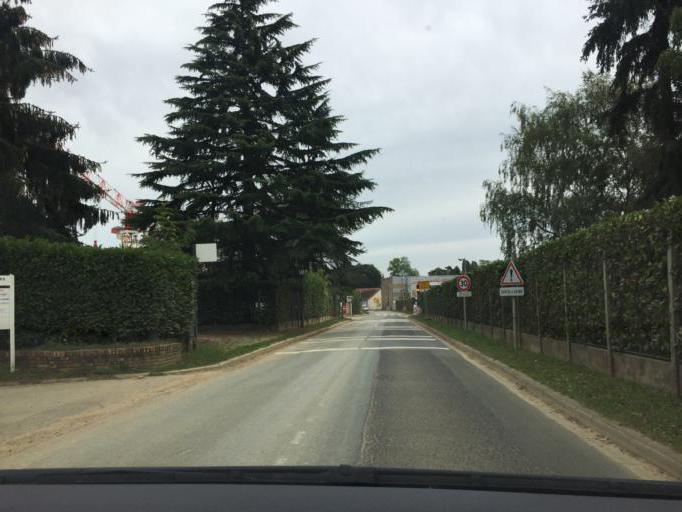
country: FR
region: Ile-de-France
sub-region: Departement des Yvelines
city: Les Loges-en-Josas
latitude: 48.7606
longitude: 2.1323
